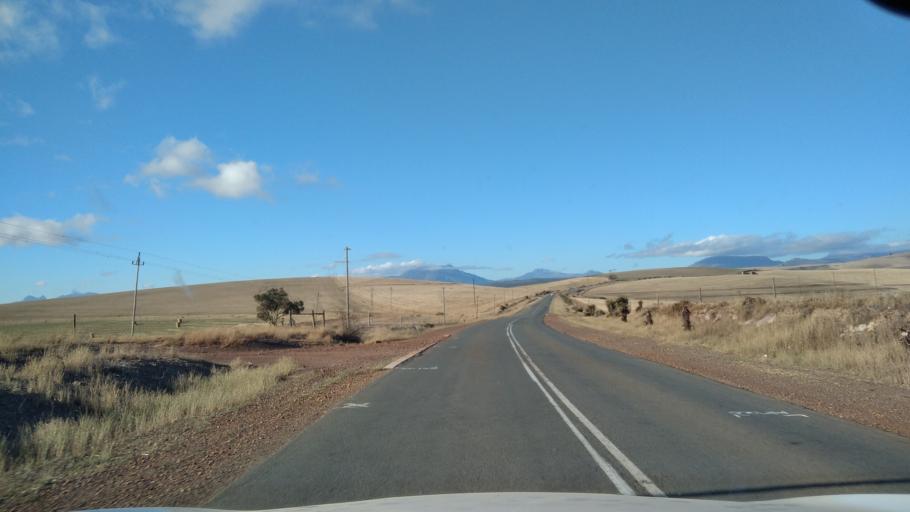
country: ZA
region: Western Cape
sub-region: Overberg District Municipality
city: Caledon
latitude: -34.1975
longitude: 19.2694
